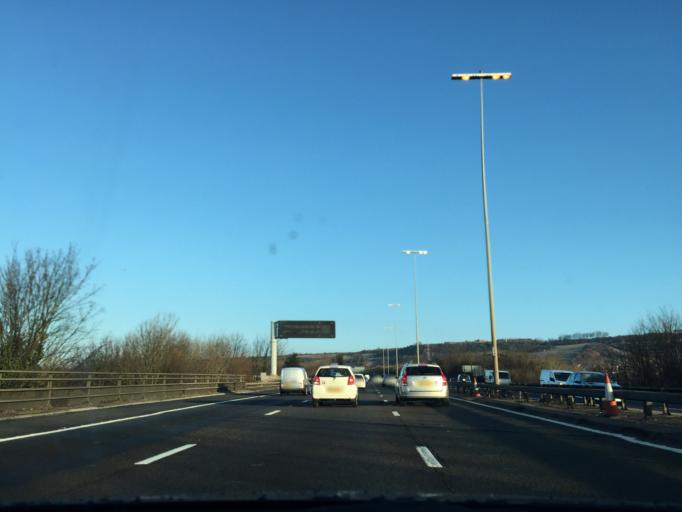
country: GB
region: England
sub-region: Portsmouth
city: Cosham
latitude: 50.8479
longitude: -1.1011
